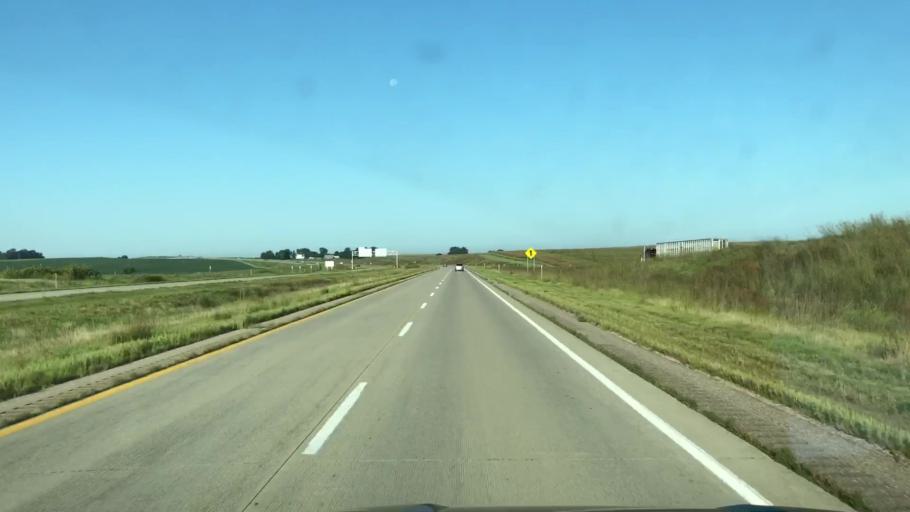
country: US
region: Iowa
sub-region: Plymouth County
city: Le Mars
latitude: 42.8181
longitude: -96.1766
